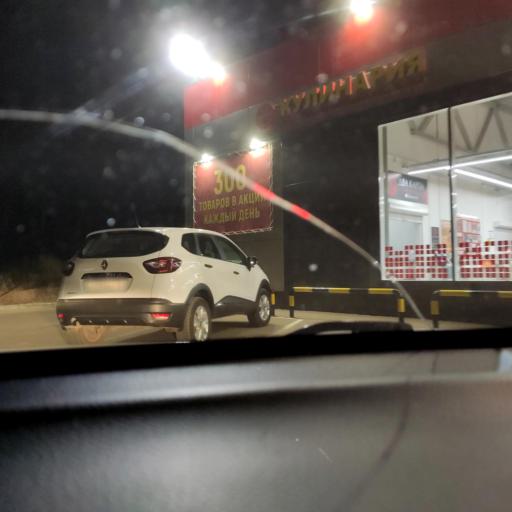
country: RU
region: Tatarstan
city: Stolbishchi
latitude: 55.7181
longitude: 49.3401
